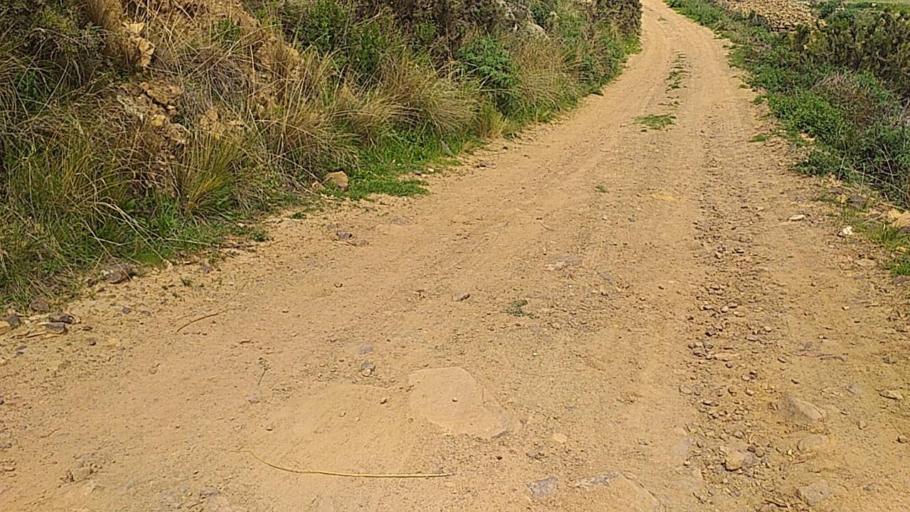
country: BO
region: La Paz
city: Batallas
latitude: -16.3262
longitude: -68.6439
